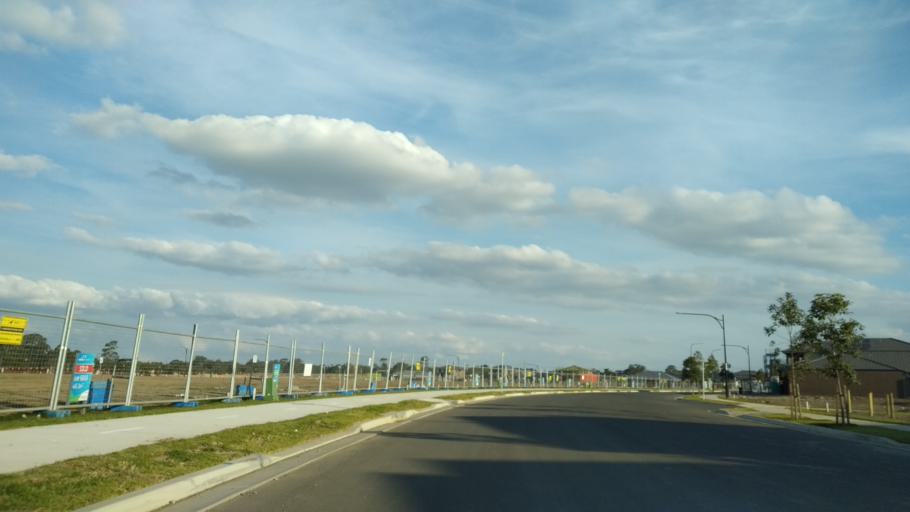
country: AU
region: New South Wales
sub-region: Penrith Municipality
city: Werrington County
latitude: -33.7312
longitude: 150.7559
